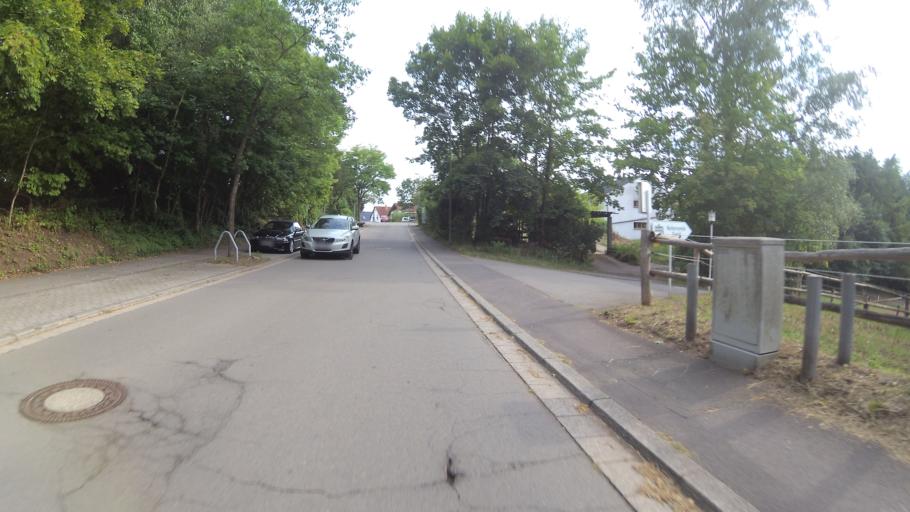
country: DE
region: Saarland
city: Homburg
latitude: 49.2751
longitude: 7.3206
